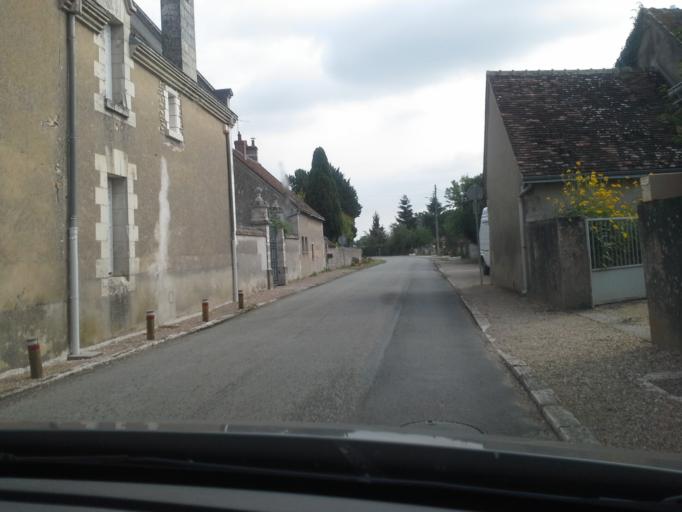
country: FR
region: Centre
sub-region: Departement du Loir-et-Cher
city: Herbault
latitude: 47.5891
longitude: 1.1995
